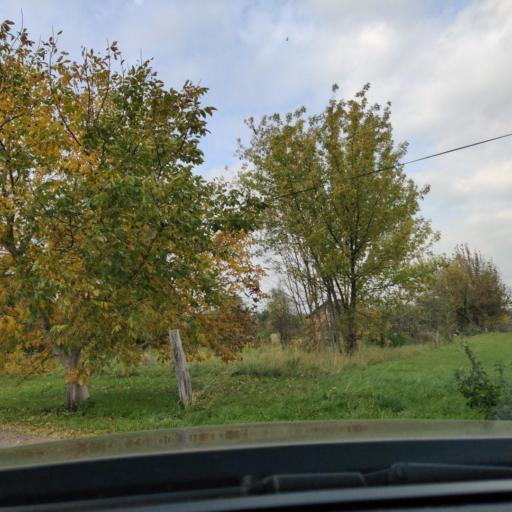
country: PL
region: Masovian Voivodeship
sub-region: Powiat sochaczewski
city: Paprotnia
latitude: 52.2377
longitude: 20.4129
